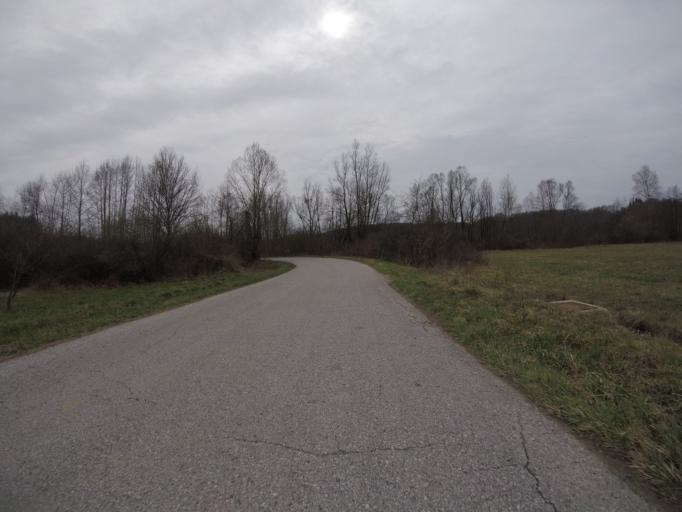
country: HR
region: Zagrebacka
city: Lukavec
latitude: 45.5666
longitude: 15.9652
